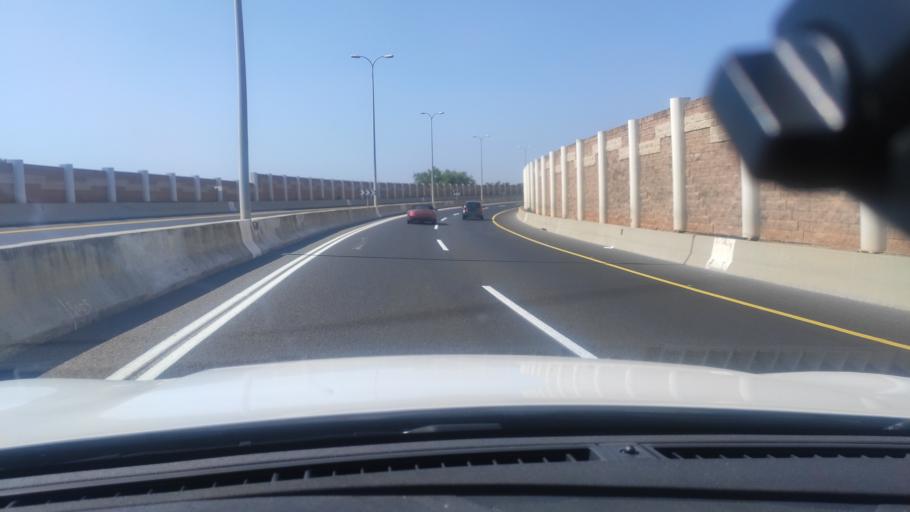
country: IL
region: Central District
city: Kfar Saba
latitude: 32.1584
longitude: 34.9264
